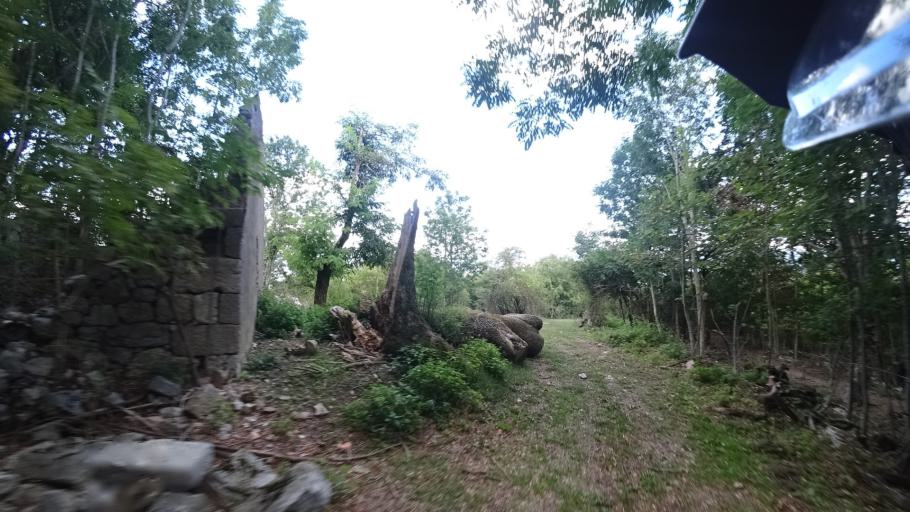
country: HR
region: Zadarska
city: Gracac
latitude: 44.3667
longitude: 16.0879
